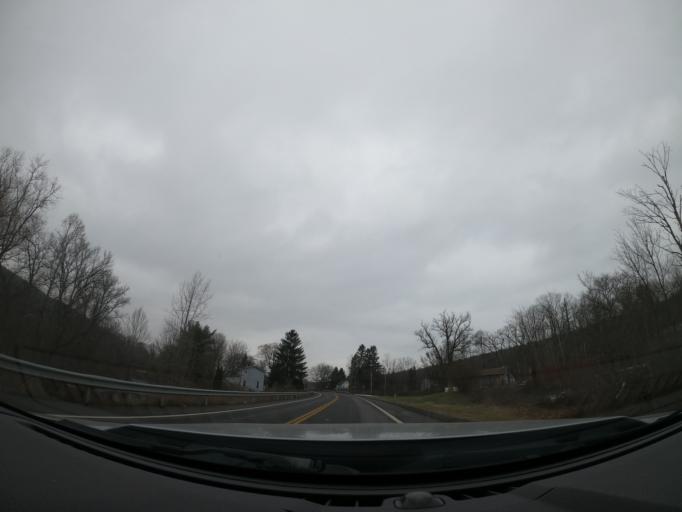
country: US
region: New York
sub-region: Cayuga County
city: Moravia
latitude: 42.6808
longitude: -76.4259
